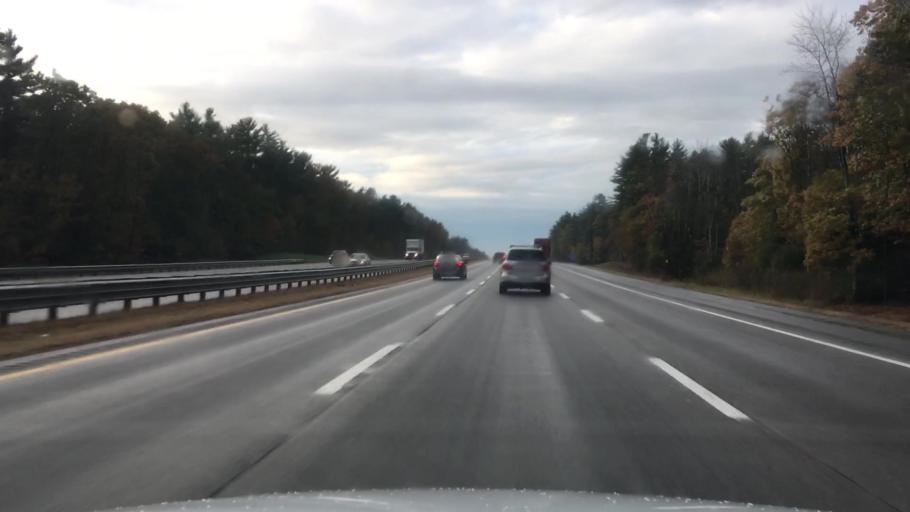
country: US
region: Maine
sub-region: Cumberland County
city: West Scarborough
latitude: 43.5633
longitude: -70.4152
